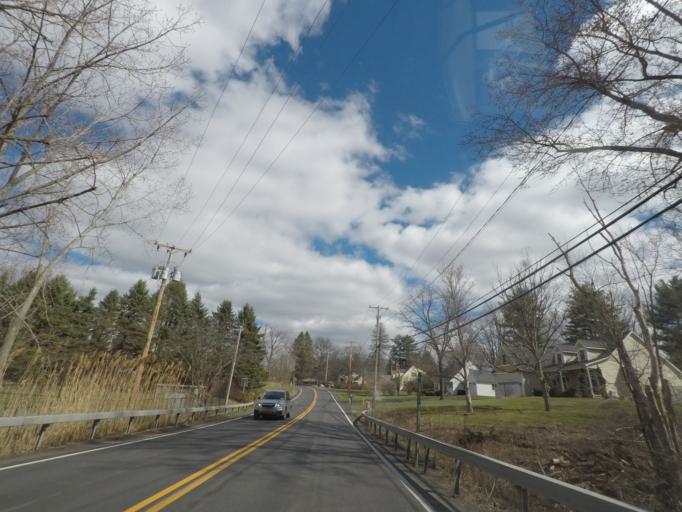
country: US
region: New York
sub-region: Albany County
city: Delmar
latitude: 42.5987
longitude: -73.7812
